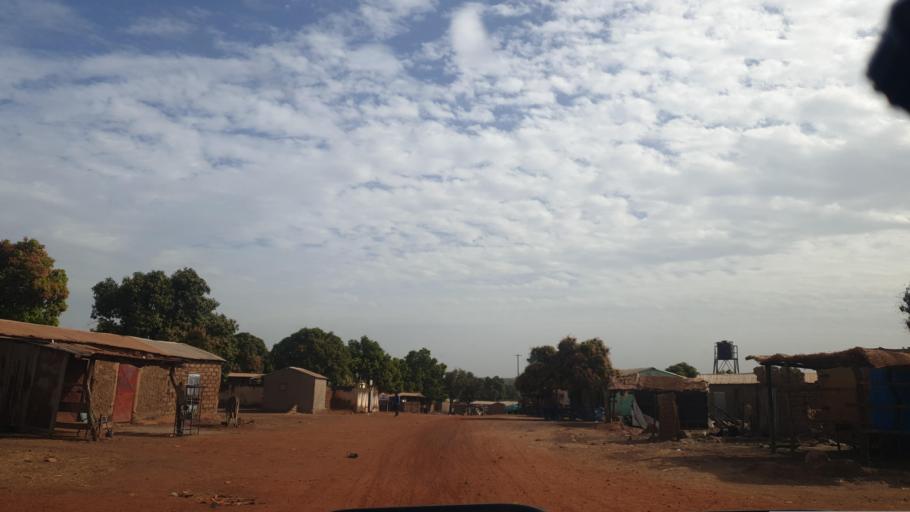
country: ML
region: Sikasso
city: Yanfolila
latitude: 11.4178
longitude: -7.9985
